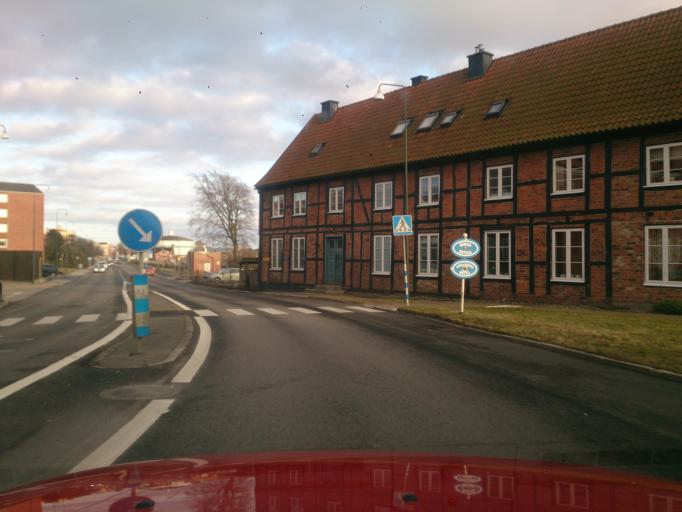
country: SE
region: Skane
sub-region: Ystads Kommun
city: Ystad
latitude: 55.4272
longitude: 13.8117
